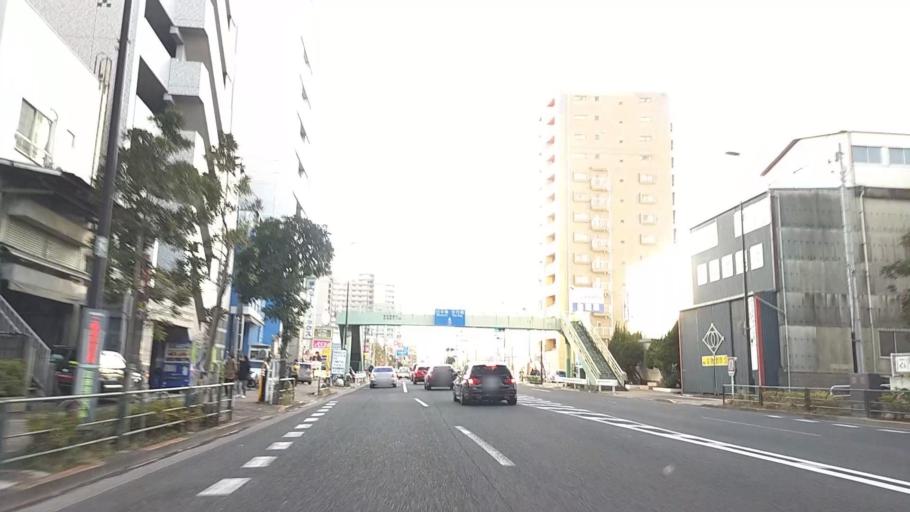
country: JP
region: Tokyo
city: Urayasu
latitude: 35.6723
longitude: 139.8385
